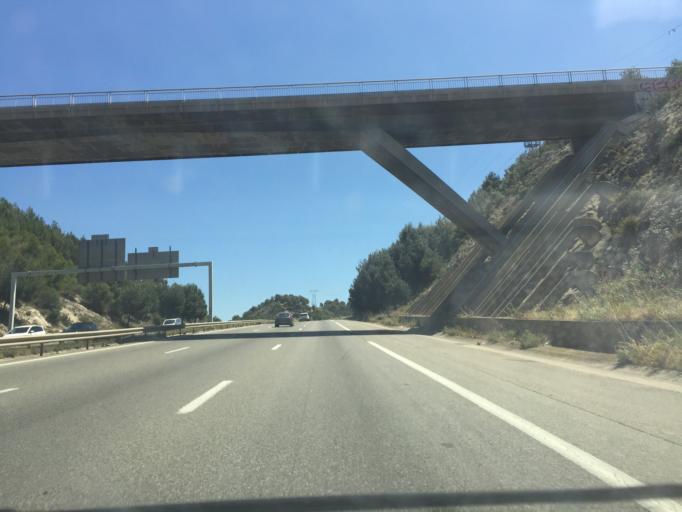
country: FR
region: Provence-Alpes-Cote d'Azur
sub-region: Departement des Bouches-du-Rhone
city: Les Pennes-Mirabeau
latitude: 43.3893
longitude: 5.3035
